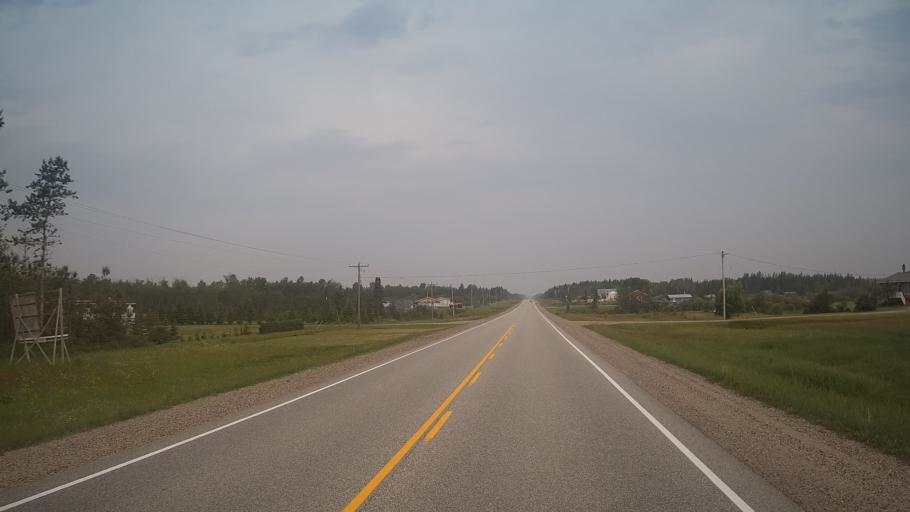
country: CA
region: Ontario
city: Hearst
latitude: 49.7164
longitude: -83.8316
